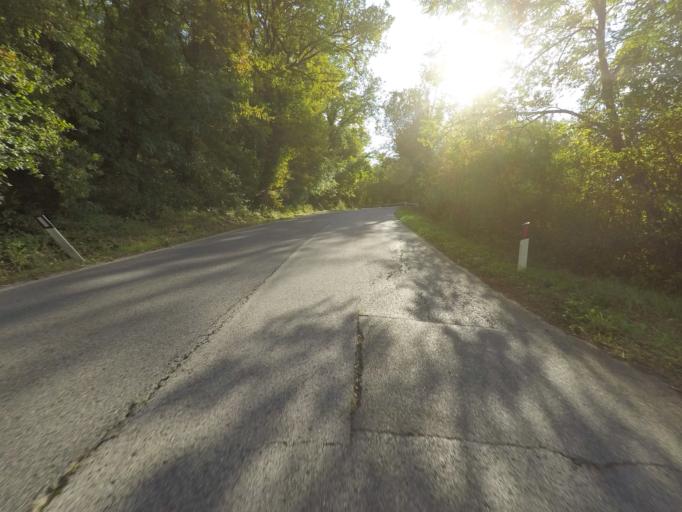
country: IT
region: Tuscany
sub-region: Provincia di Siena
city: Radda in Chianti
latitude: 43.4978
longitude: 11.3930
